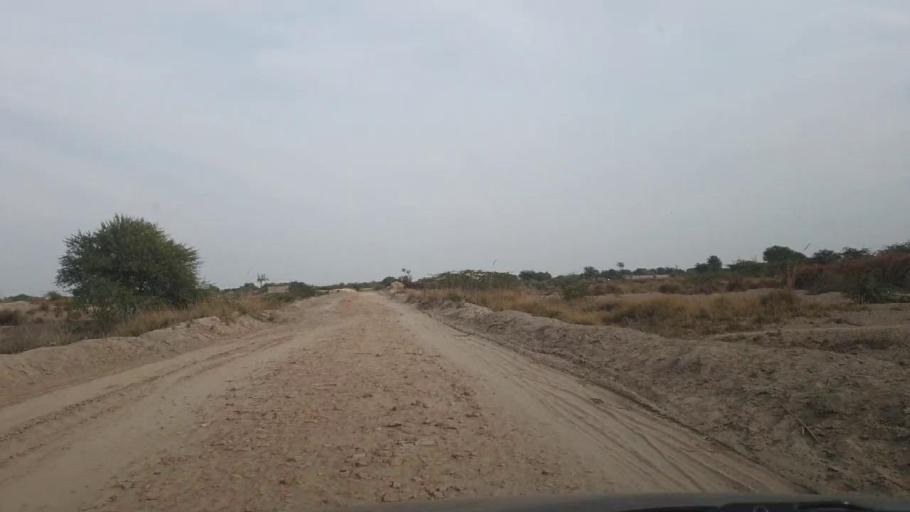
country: PK
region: Sindh
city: Shahpur Chakar
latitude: 26.1168
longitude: 68.5088
